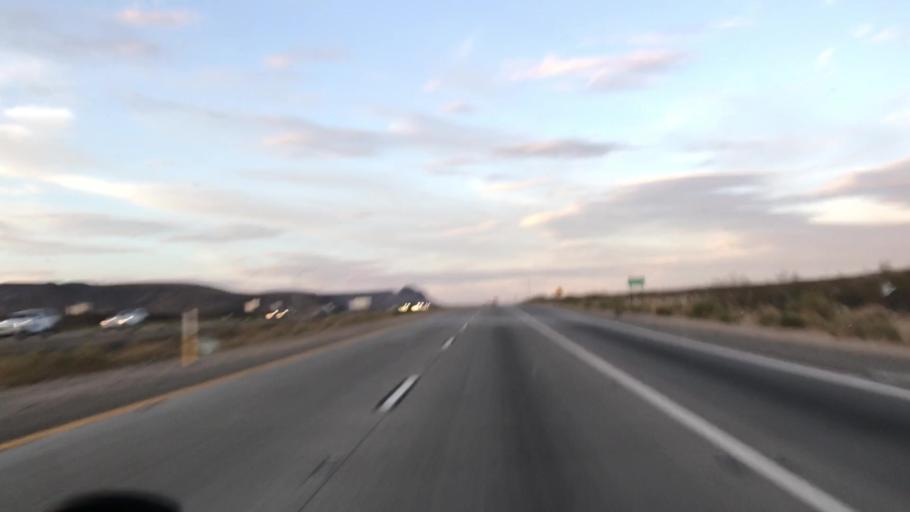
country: US
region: Nevada
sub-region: Clark County
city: Sandy Valley
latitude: 35.3745
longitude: -115.8907
